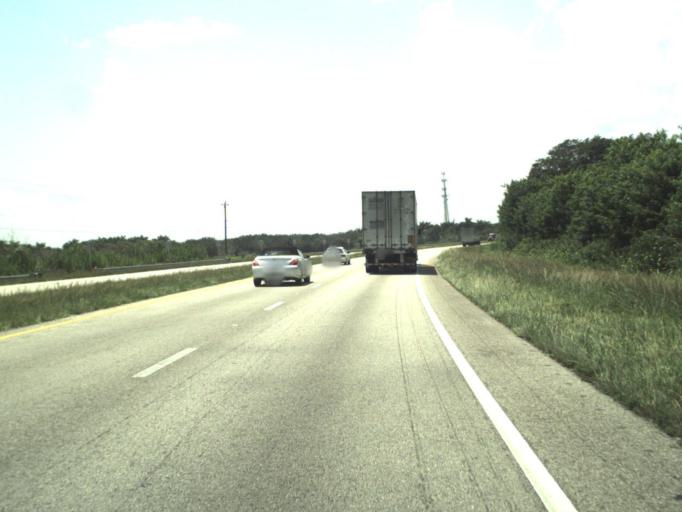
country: US
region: Florida
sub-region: Palm Beach County
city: South Bay
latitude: 26.6962
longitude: -80.8163
